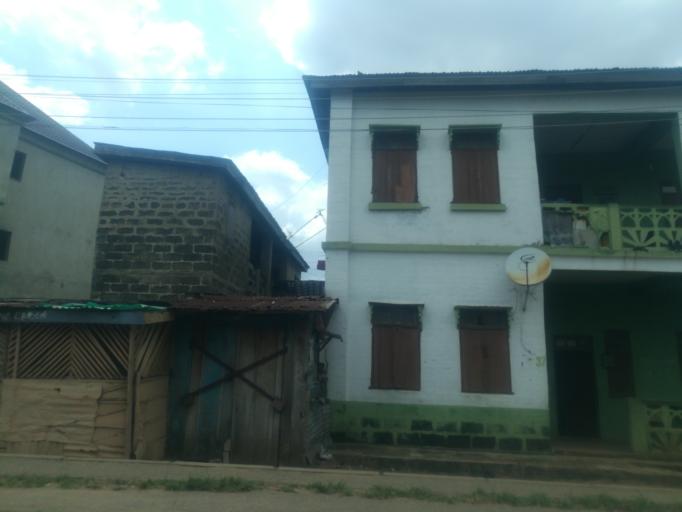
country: NG
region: Oyo
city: Ibadan
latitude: 7.3960
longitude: 3.8840
